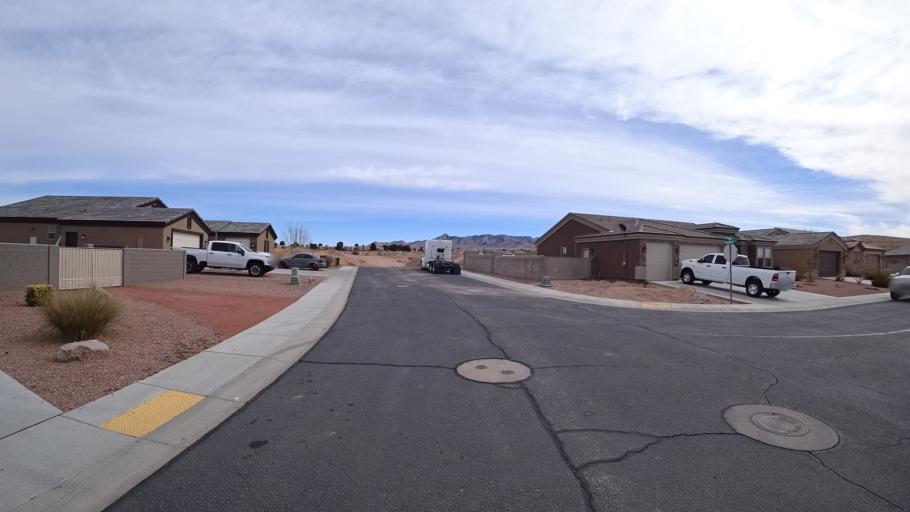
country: US
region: Arizona
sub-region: Mohave County
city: Kingman
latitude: 35.1871
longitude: -114.0162
